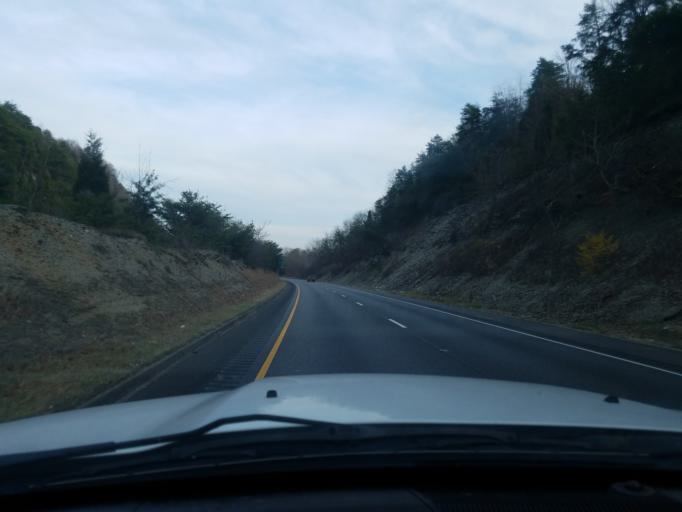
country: US
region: Indiana
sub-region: Floyd County
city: New Albany
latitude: 38.3015
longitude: -85.8707
